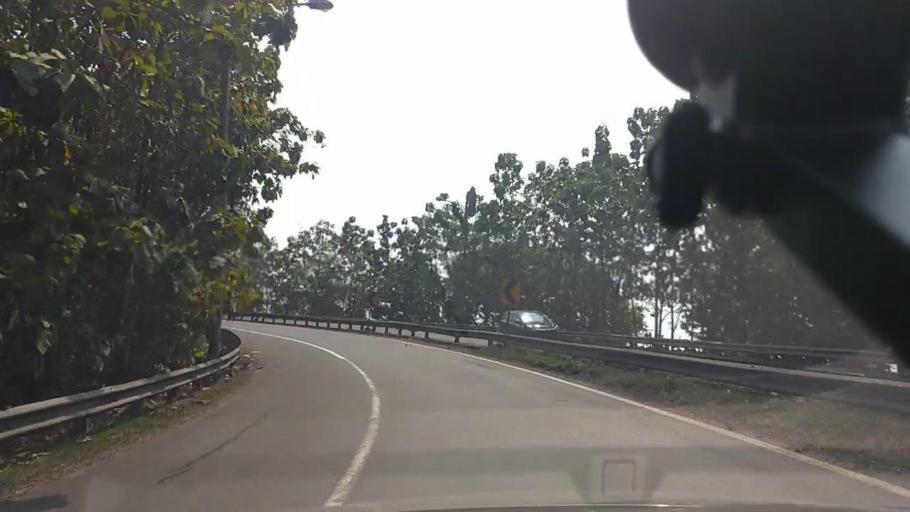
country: ID
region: Banten
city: Serang
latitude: -6.1143
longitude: 106.1864
